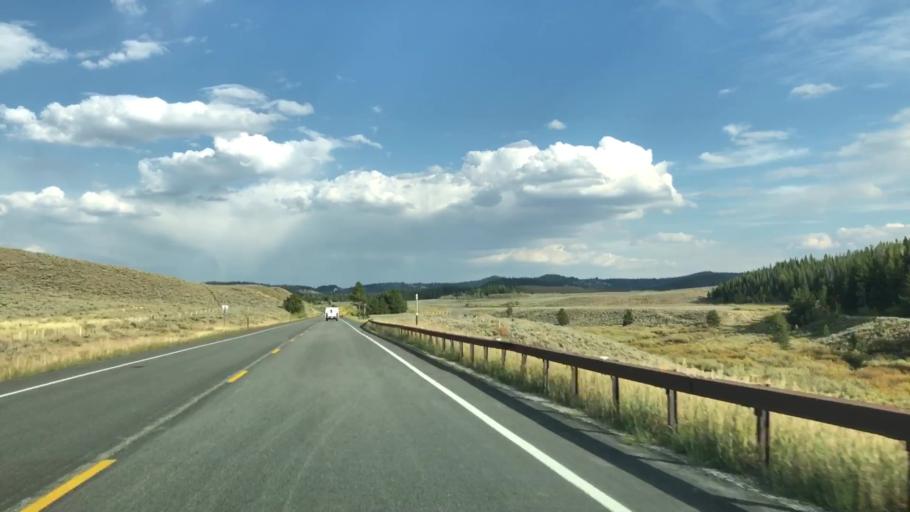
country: US
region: Wyoming
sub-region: Sublette County
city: Pinedale
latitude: 43.1505
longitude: -110.2754
